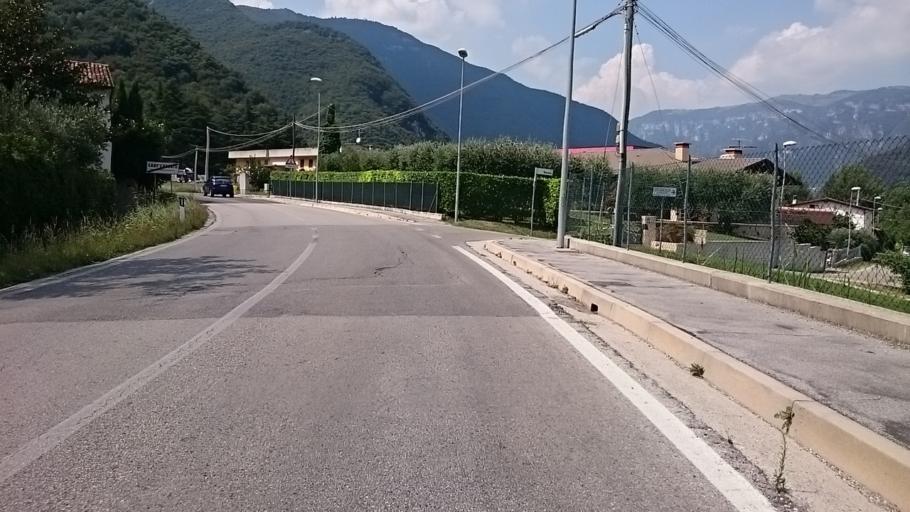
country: IT
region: Veneto
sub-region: Provincia di Vicenza
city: Pove del Grappa
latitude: 45.7869
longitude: 11.7207
